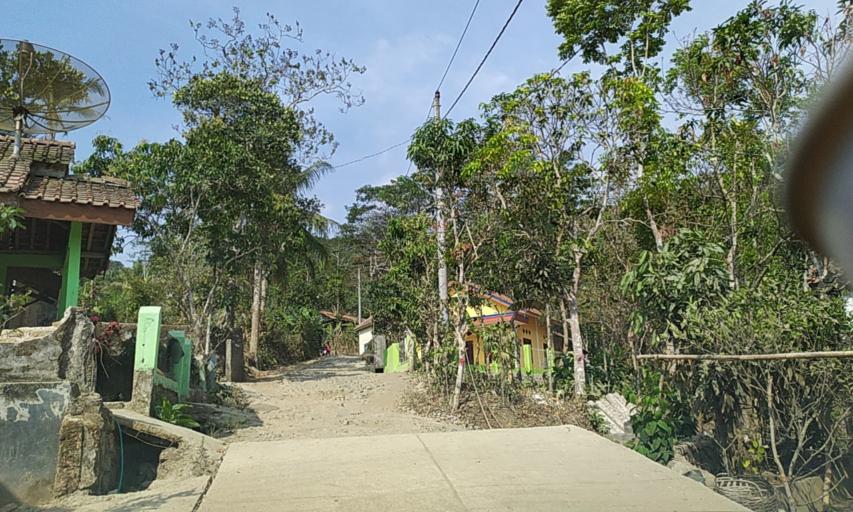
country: ID
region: Central Java
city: Jambuluwuk
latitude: -7.3064
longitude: 108.9105
